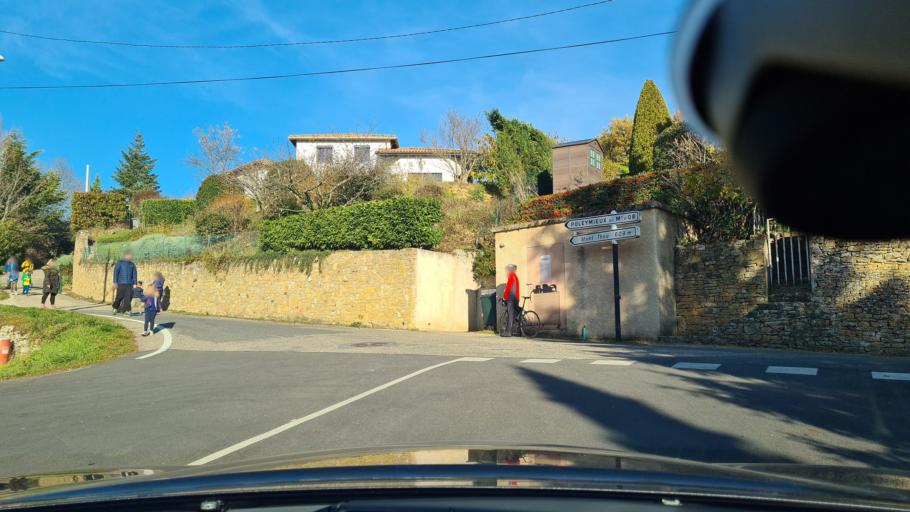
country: FR
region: Rhone-Alpes
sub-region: Departement du Rhone
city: Fontaines-sur-Saone
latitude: 45.8263
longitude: 4.8100
